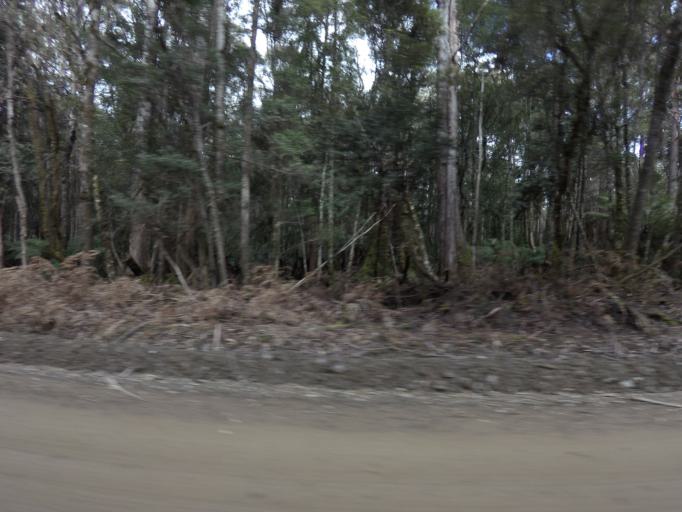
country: AU
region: Tasmania
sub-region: Huon Valley
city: Geeveston
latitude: -43.4015
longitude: 146.8623
